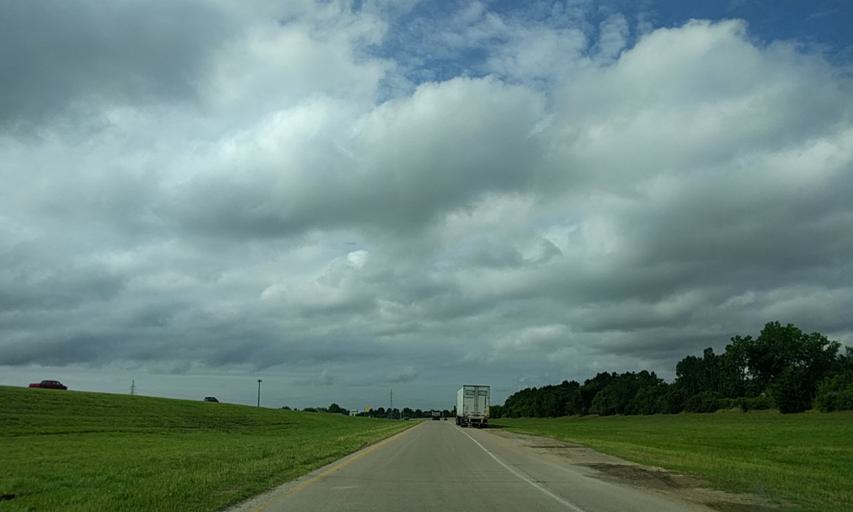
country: US
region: Oklahoma
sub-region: Tulsa County
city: Owasso
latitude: 36.3074
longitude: -95.8225
